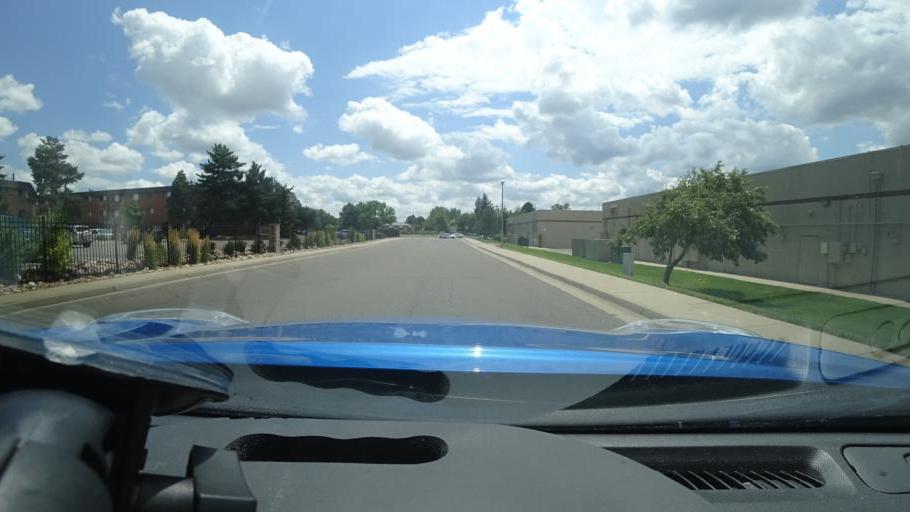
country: US
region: Colorado
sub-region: Adams County
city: Aurora
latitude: 39.6976
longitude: -104.8430
